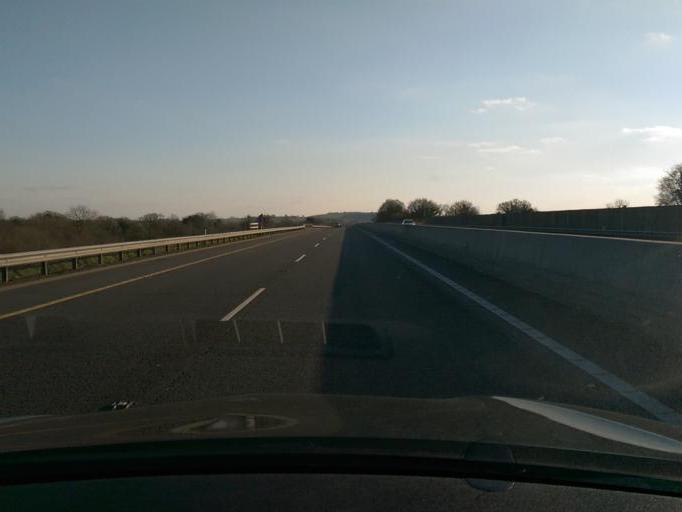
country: IE
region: Leinster
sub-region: Laois
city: Mountrath
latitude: 52.9547
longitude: -7.4426
